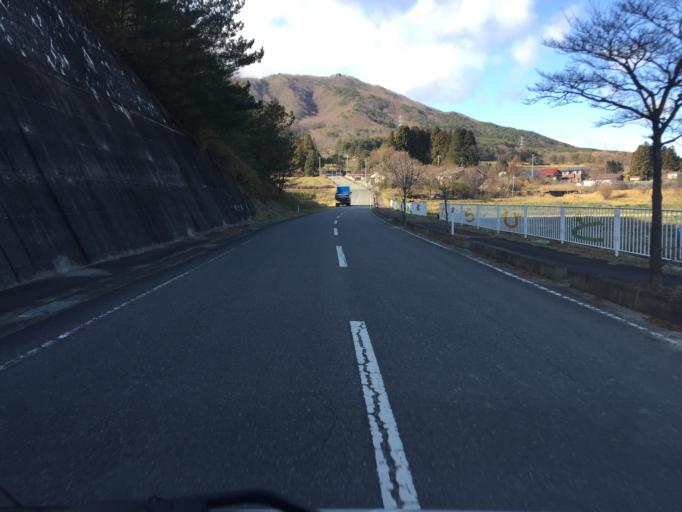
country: JP
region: Fukushima
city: Ishikawa
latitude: 37.2576
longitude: 140.5552
